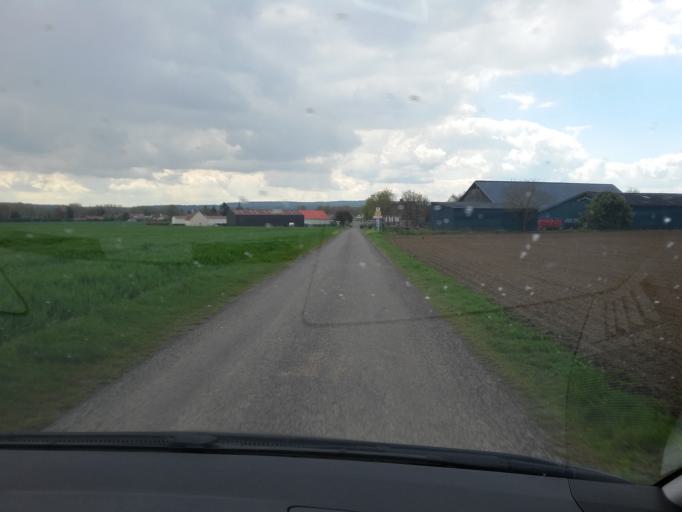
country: FR
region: Picardie
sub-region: Departement de l'Oise
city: Chevrieres
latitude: 49.3545
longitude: 2.6826
